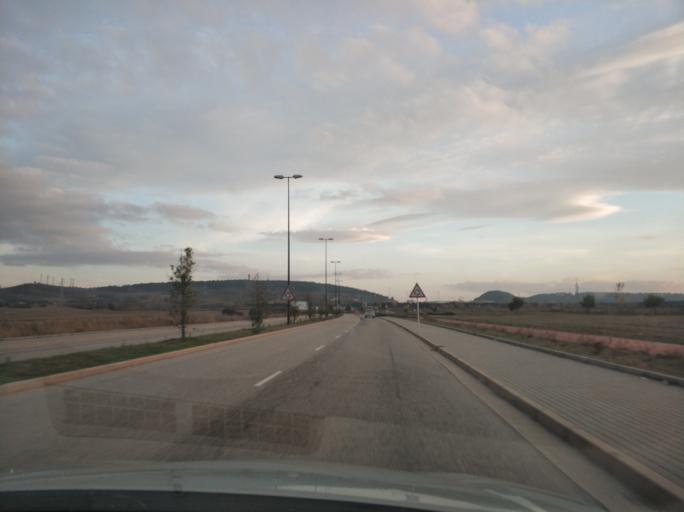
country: ES
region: Castille and Leon
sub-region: Provincia de Burgos
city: Burgos
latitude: 42.3730
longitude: -3.6992
